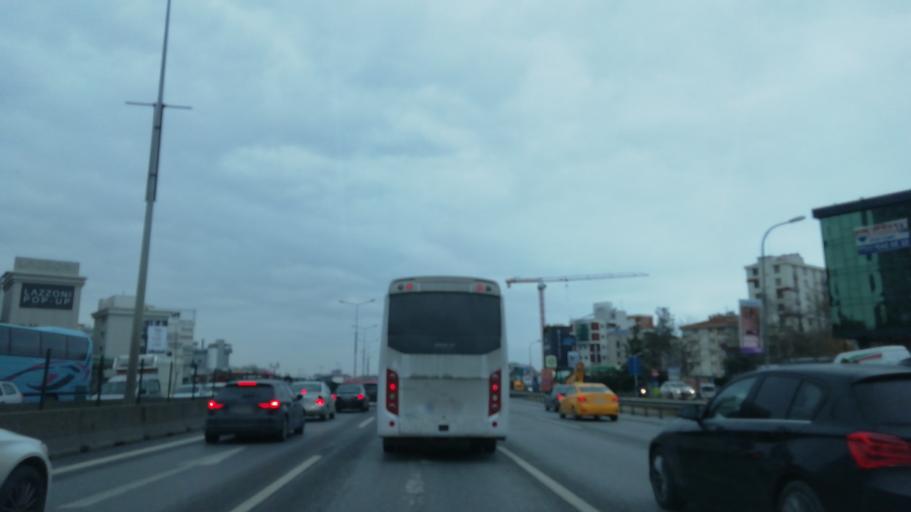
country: TR
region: Istanbul
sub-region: Atasehir
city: Atasehir
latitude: 40.9677
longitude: 29.1031
